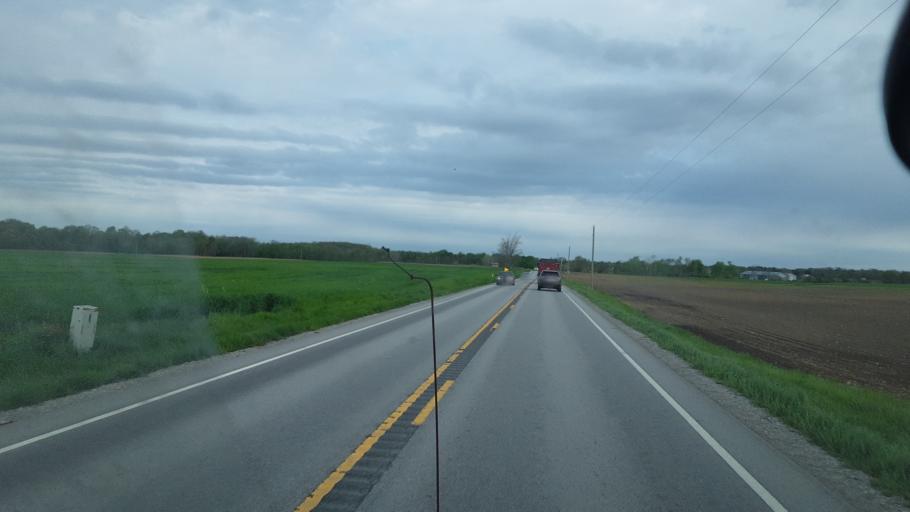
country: US
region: Indiana
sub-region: Whitley County
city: Tri-Lakes
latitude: 41.2749
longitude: -85.4136
